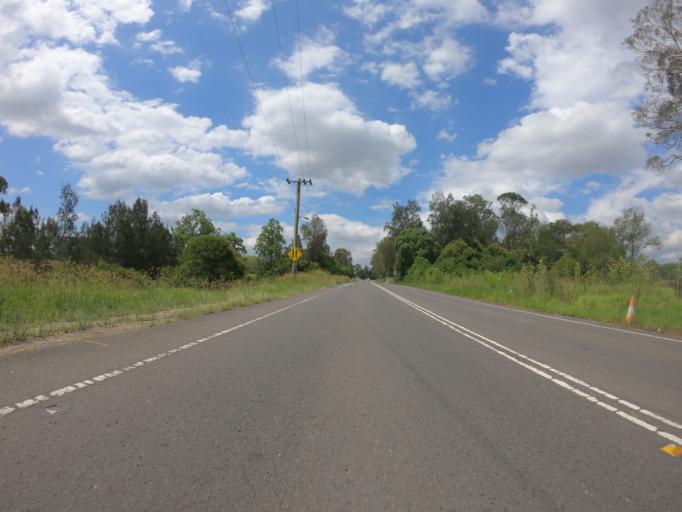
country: AU
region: New South Wales
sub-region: Blacktown
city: Mount Druitt
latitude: -33.8055
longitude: 150.7661
